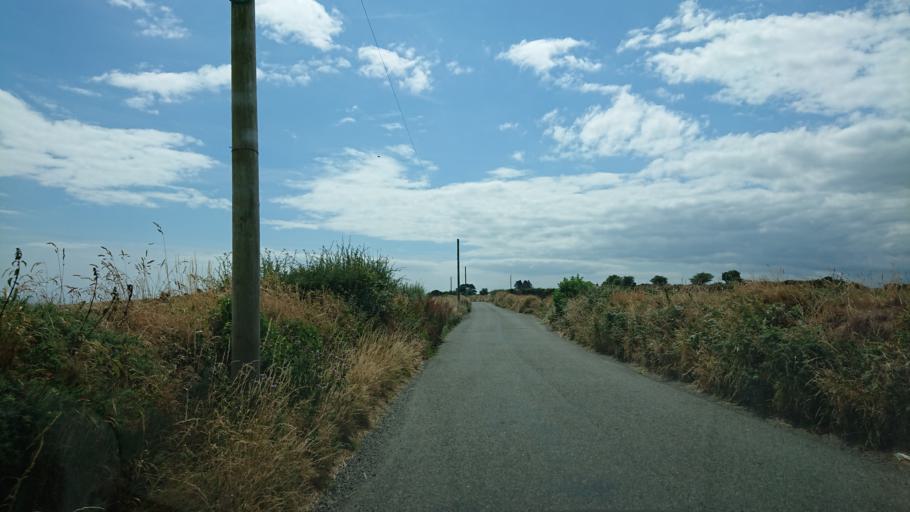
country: IE
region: Munster
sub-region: Waterford
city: Portlaw
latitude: 52.1938
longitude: -7.3287
